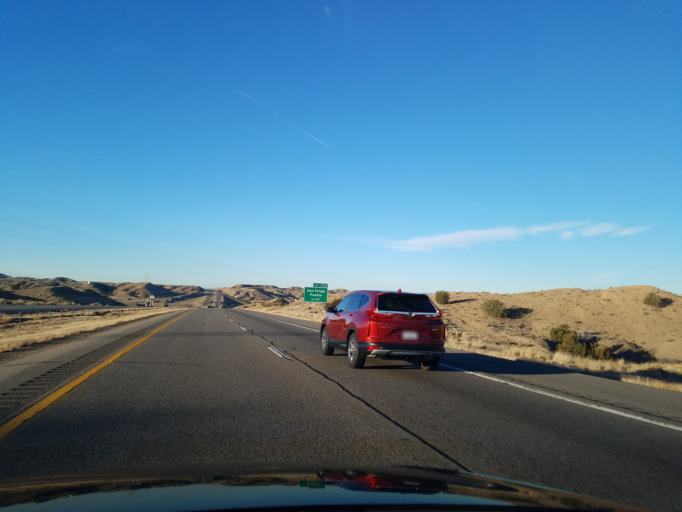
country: US
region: New Mexico
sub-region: Sandoval County
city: San Felipe Pueblo
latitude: 35.4253
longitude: -106.3917
